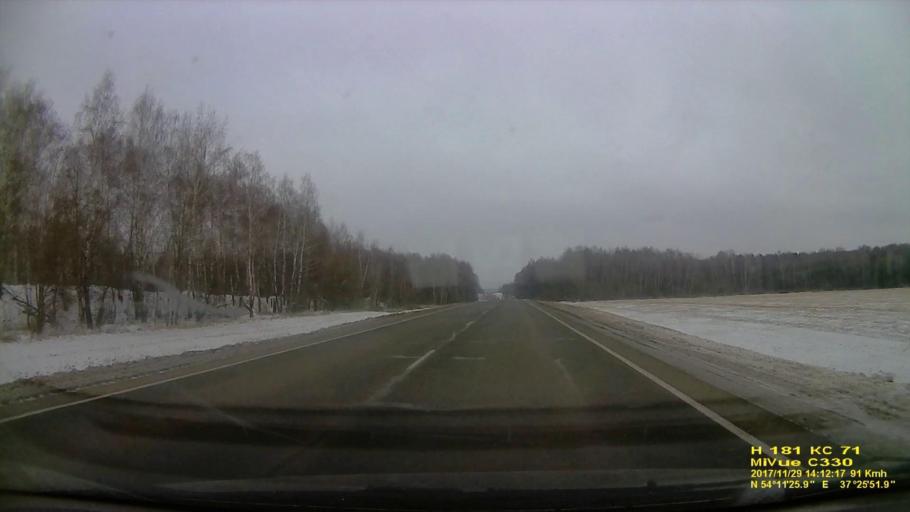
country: RU
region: Tula
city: Barsuki
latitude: 54.1903
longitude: 37.4315
